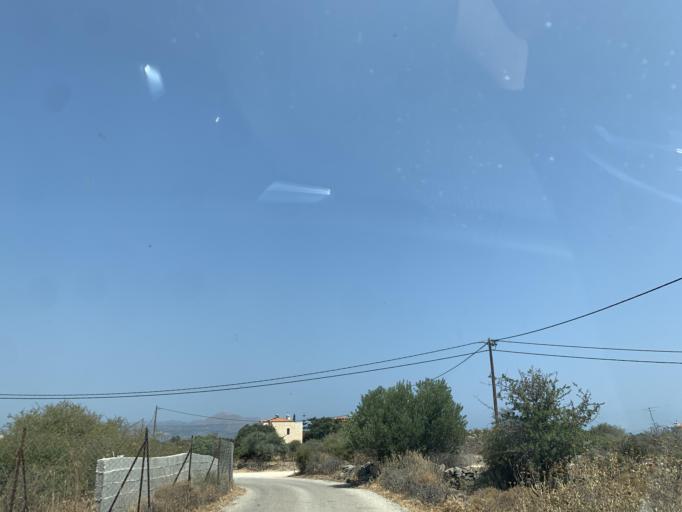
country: GR
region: Crete
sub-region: Nomos Chanias
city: Kalivai
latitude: 35.4523
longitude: 24.2339
